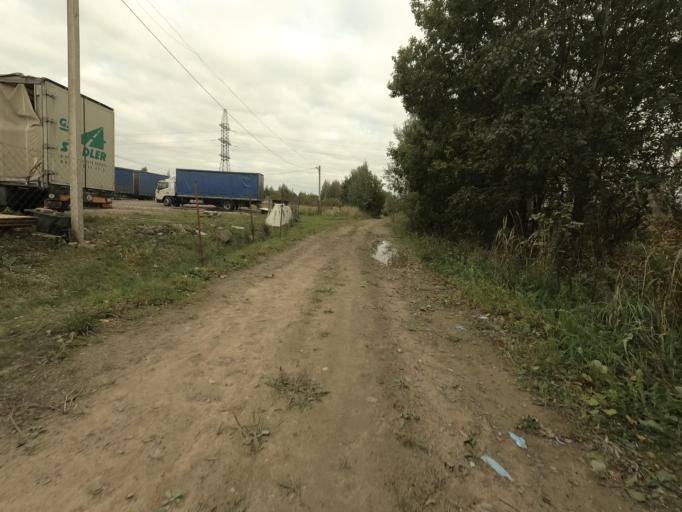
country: RU
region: St.-Petersburg
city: Metallostroy
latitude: 59.8217
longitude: 30.5284
